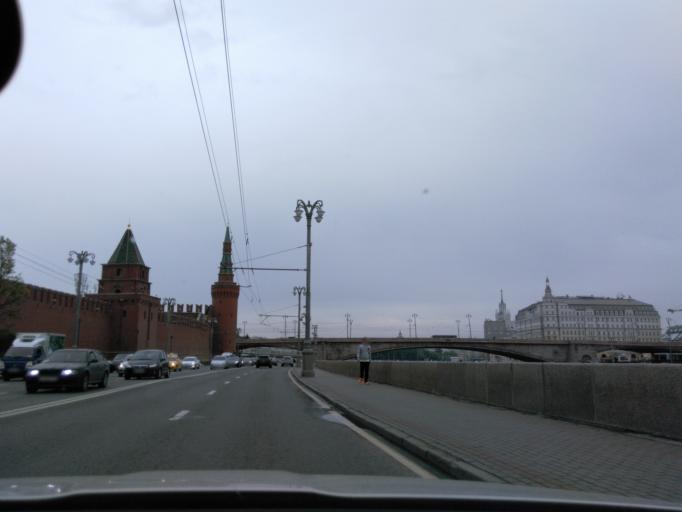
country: RU
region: Moscow
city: Moscow
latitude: 55.7492
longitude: 37.6203
